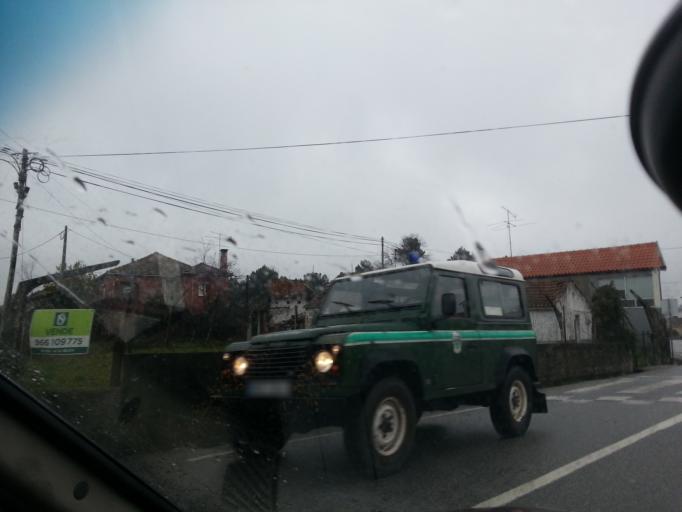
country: PT
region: Viseu
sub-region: Viseu
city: Rio de Loba
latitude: 40.6505
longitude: -7.8734
